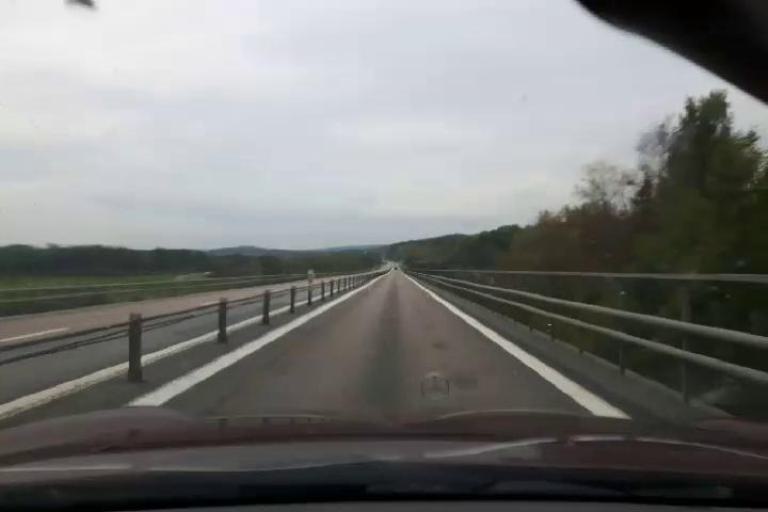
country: SE
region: Vaesternorrland
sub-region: Haernoesands Kommun
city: Haernoesand
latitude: 62.8578
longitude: 18.0211
